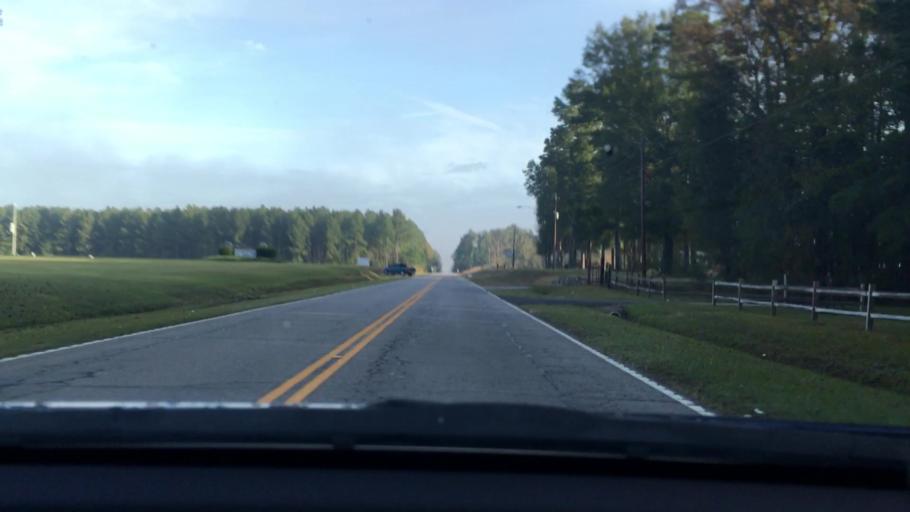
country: US
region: South Carolina
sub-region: Sumter County
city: East Sumter
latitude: 33.9705
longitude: -80.3002
